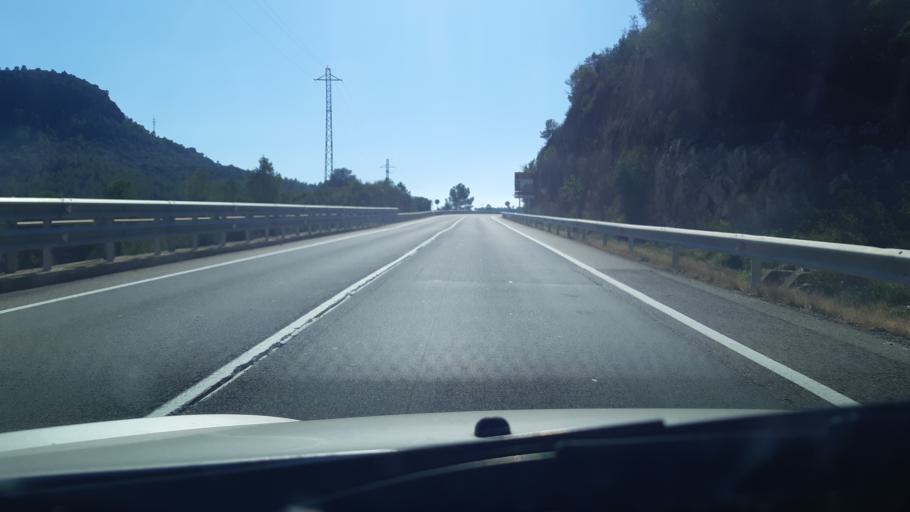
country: ES
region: Catalonia
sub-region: Provincia de Tarragona
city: Tivenys
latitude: 40.9399
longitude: 0.4889
